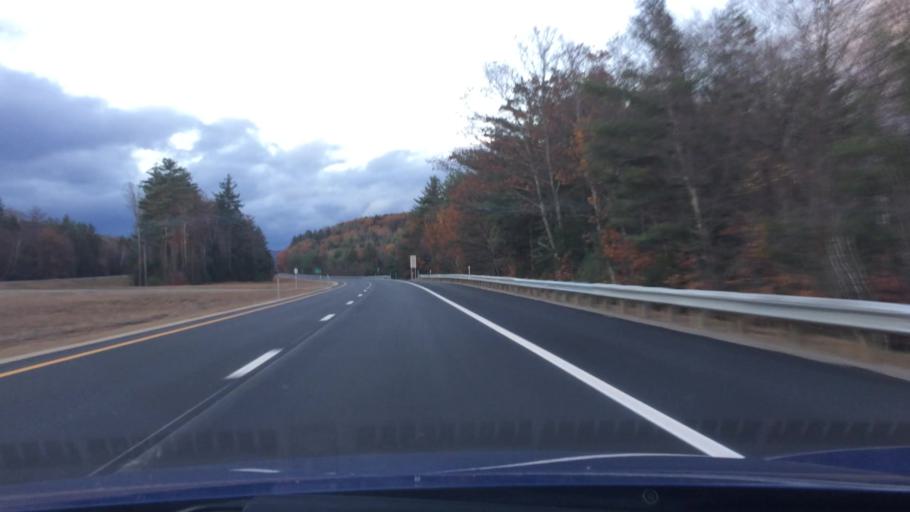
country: US
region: New Hampshire
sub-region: Grafton County
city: Thornton
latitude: 43.8783
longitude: -71.6750
